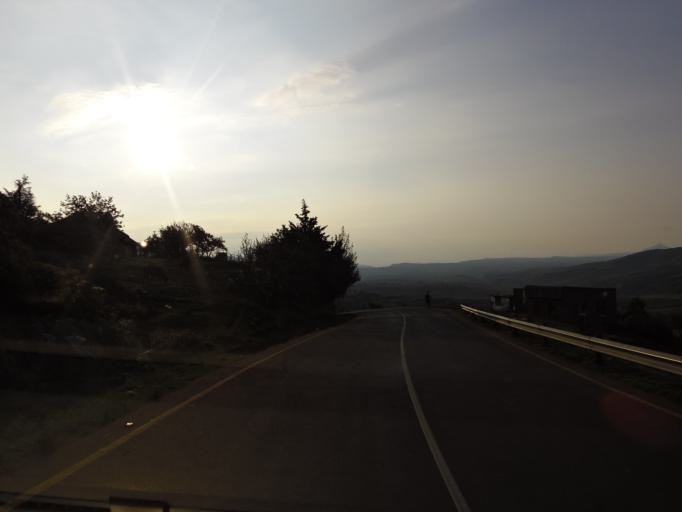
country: LS
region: Butha-Buthe
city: Butha-Buthe
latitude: -29.0361
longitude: 28.2957
